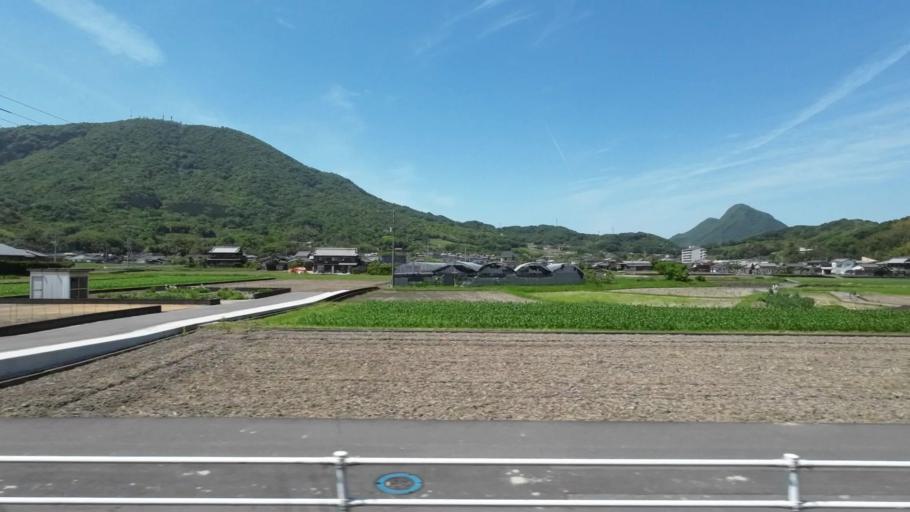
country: JP
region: Kagawa
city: Marugame
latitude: 34.2171
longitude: 133.7983
